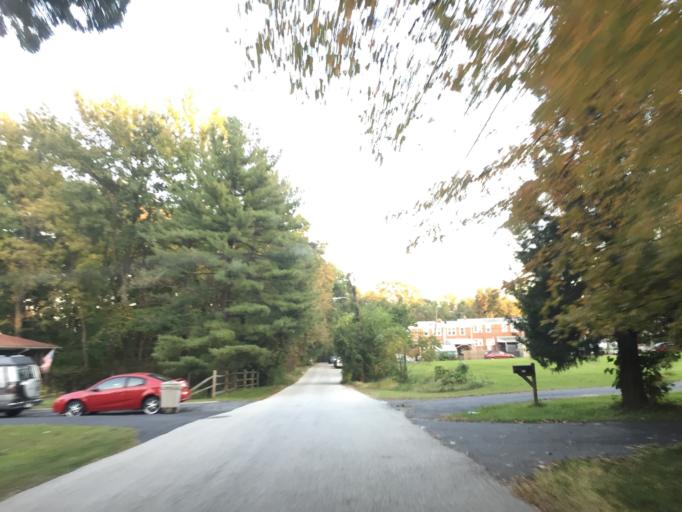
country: US
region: Maryland
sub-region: Baltimore County
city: Essex
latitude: 39.3201
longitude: -76.4618
